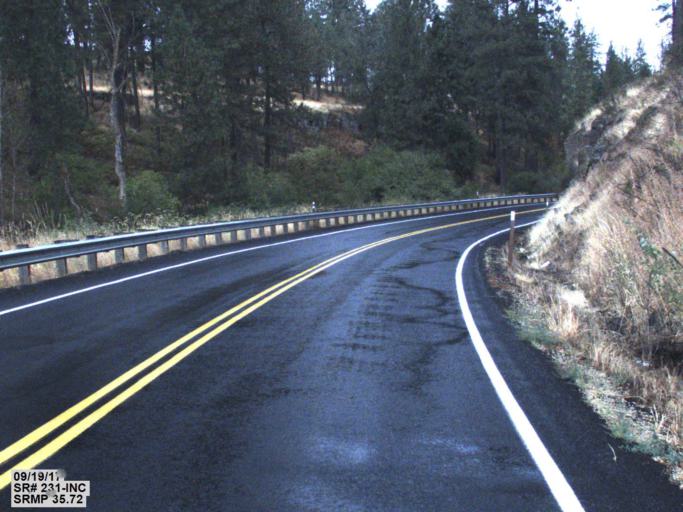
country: US
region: Washington
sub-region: Spokane County
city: Medical Lake
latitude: 47.7344
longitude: -117.8732
